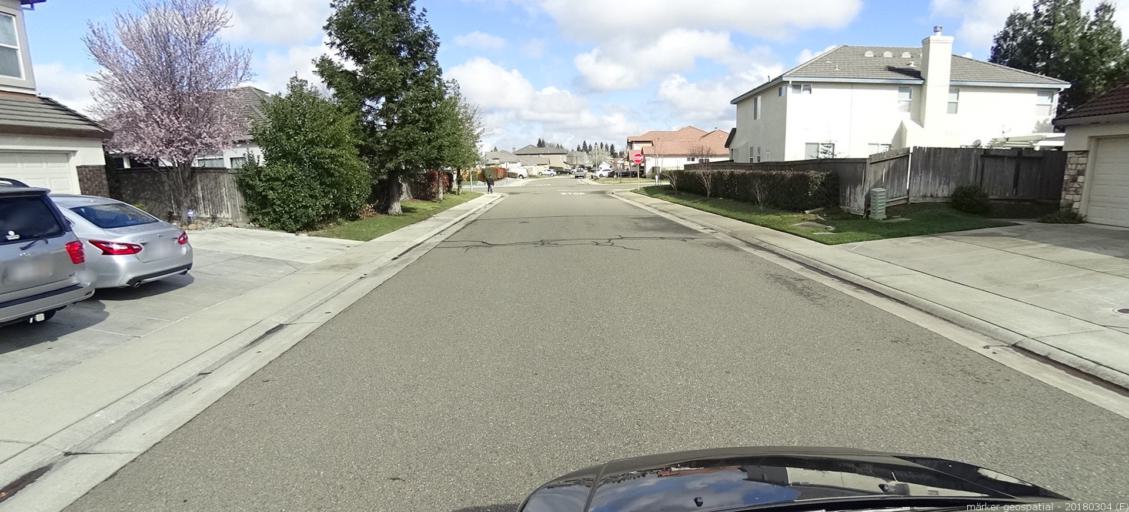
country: US
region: California
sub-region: Sacramento County
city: Vineyard
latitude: 38.4557
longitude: -121.3181
